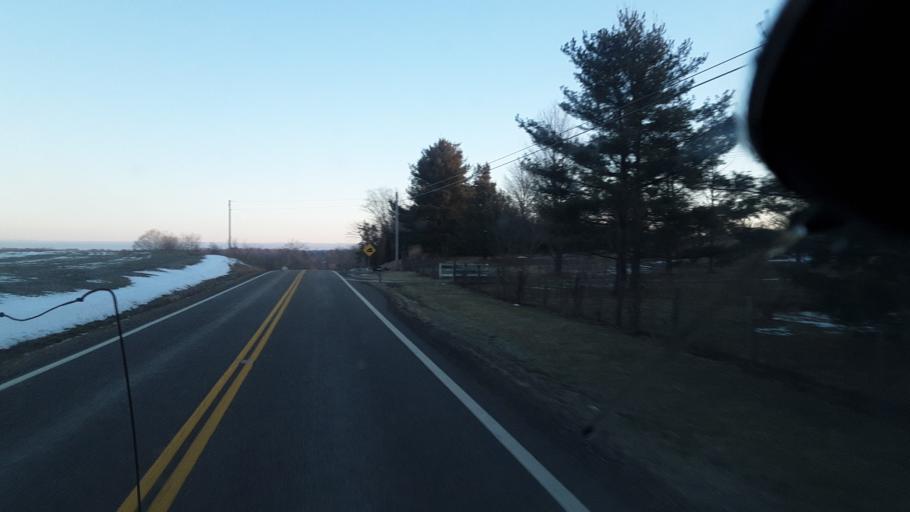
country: US
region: Ohio
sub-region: Perry County
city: Somerset
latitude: 39.7759
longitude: -82.3026
